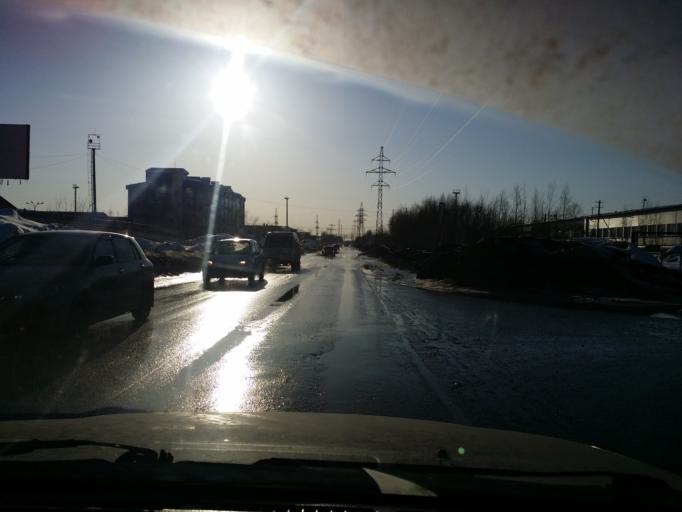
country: RU
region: Khanty-Mansiyskiy Avtonomnyy Okrug
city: Nizhnevartovsk
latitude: 60.9333
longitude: 76.5394
